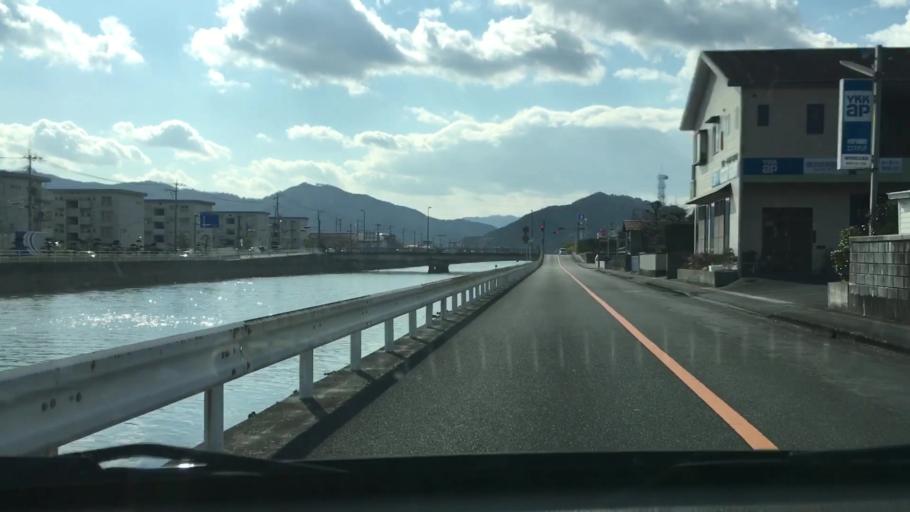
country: JP
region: Oita
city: Saiki
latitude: 32.9576
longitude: 131.9101
